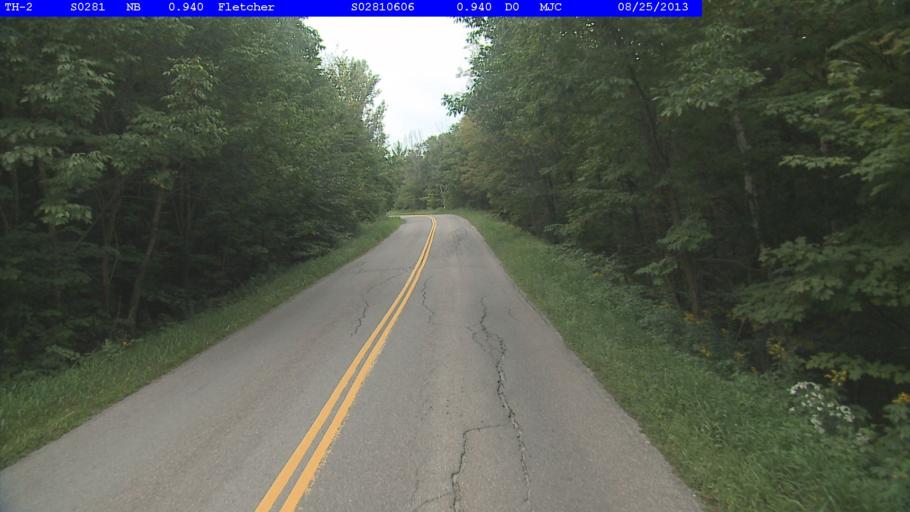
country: US
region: Vermont
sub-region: Chittenden County
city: Milton
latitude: 44.6922
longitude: -72.9271
